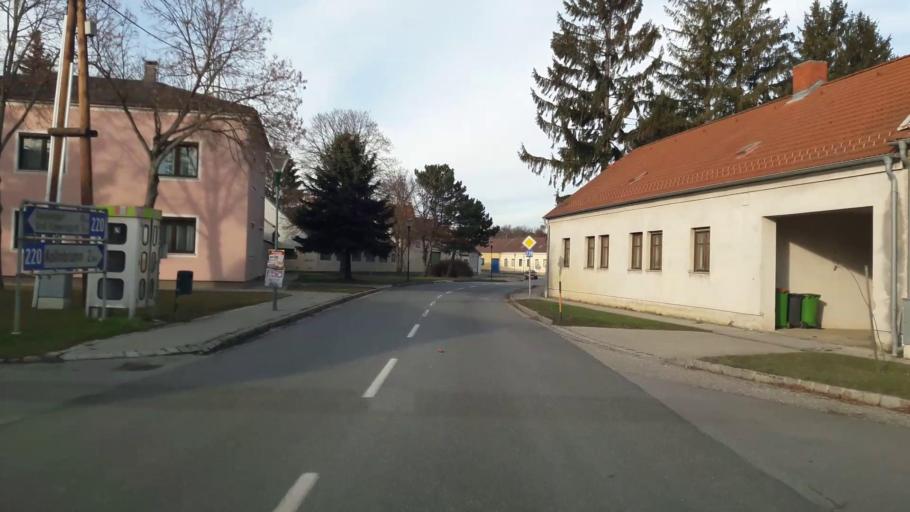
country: AT
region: Lower Austria
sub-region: Politischer Bezirk Ganserndorf
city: Bad Pirawarth
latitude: 48.4493
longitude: 16.6038
